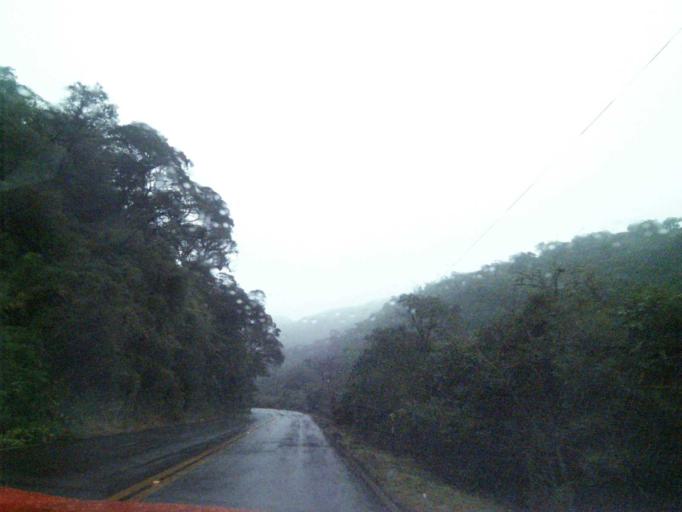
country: BR
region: Santa Catarina
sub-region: Anitapolis
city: Anitapolis
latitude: -27.7601
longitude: -49.0373
